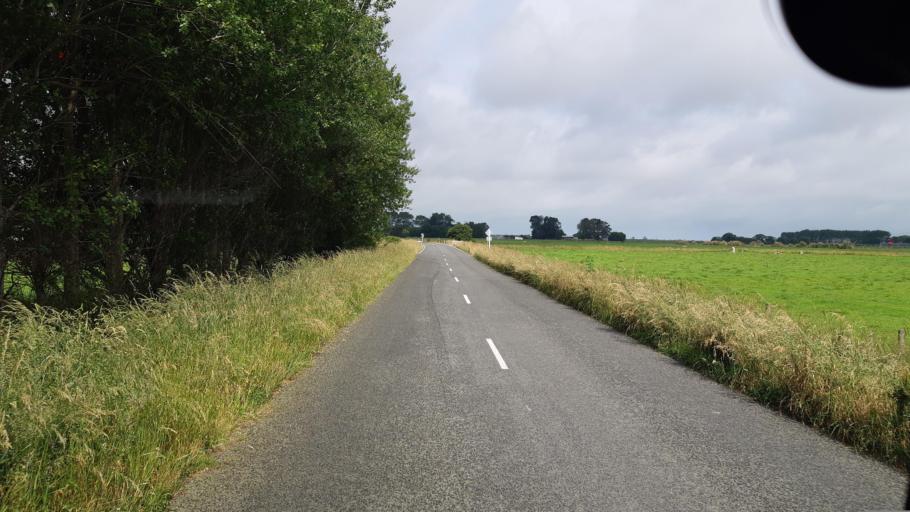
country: NZ
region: Canterbury
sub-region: Timaru District
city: Timaru
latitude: -44.2466
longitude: 171.3290
